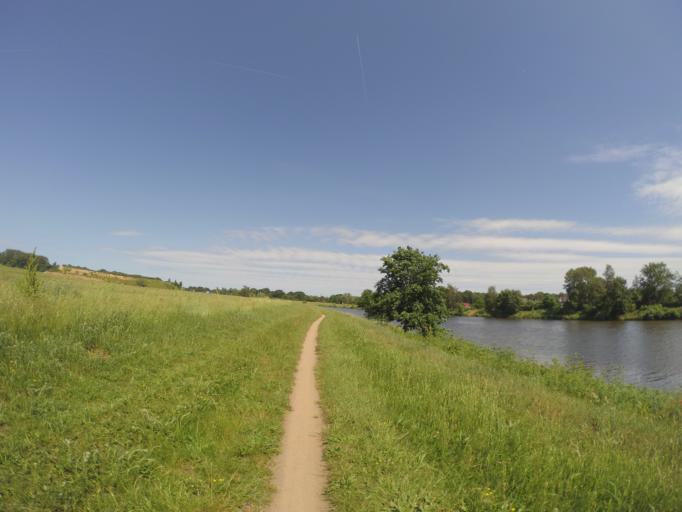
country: CZ
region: Central Bohemia
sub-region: Okres Nymburk
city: Sadska
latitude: 50.1627
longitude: 14.9714
